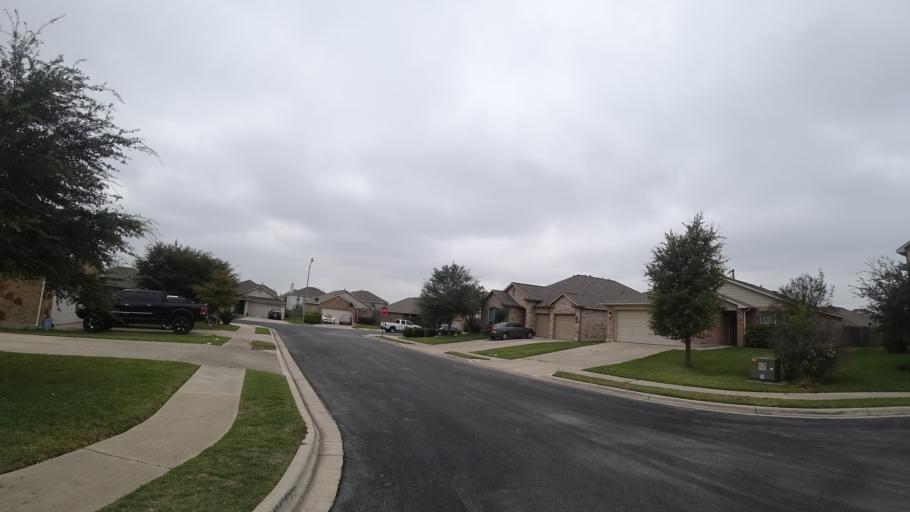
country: US
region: Texas
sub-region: Travis County
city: Pflugerville
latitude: 30.3745
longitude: -97.6483
